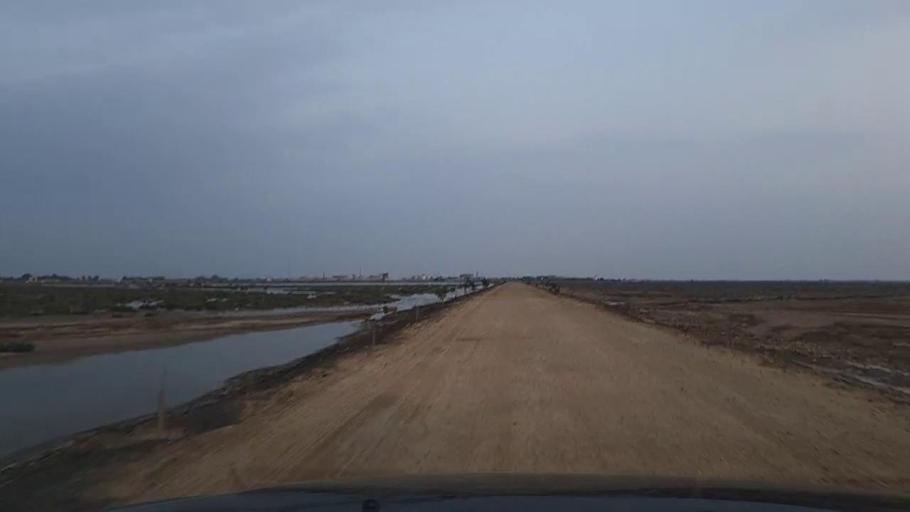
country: PK
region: Sindh
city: Jati
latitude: 24.4953
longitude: 68.3868
